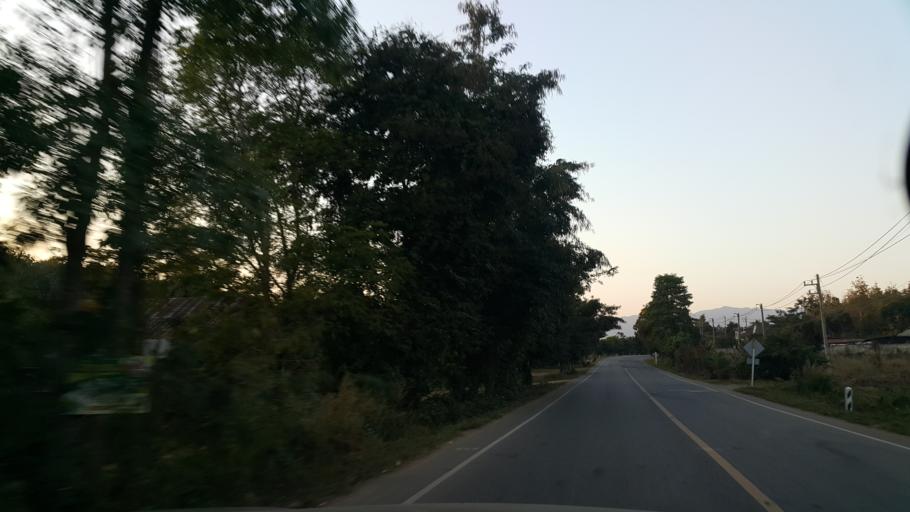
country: TH
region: Phrae
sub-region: Amphoe Wang Chin
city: Wang Chin
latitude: 17.8458
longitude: 99.6295
